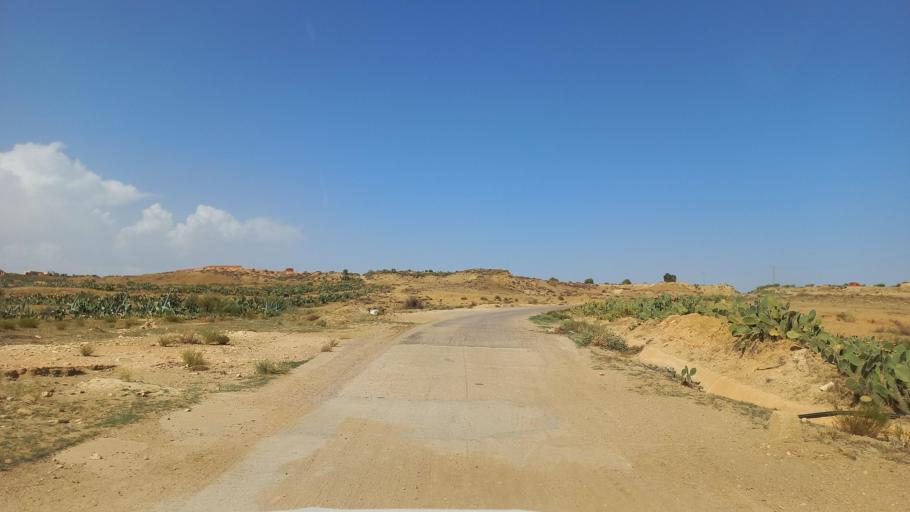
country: TN
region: Al Qasrayn
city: Kasserine
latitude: 35.2062
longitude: 9.0384
